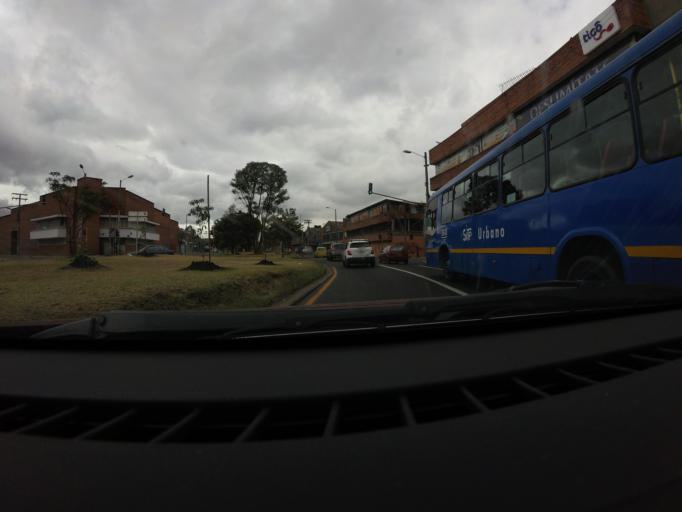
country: CO
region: Bogota D.C.
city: Bogota
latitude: 4.6288
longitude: -74.0953
